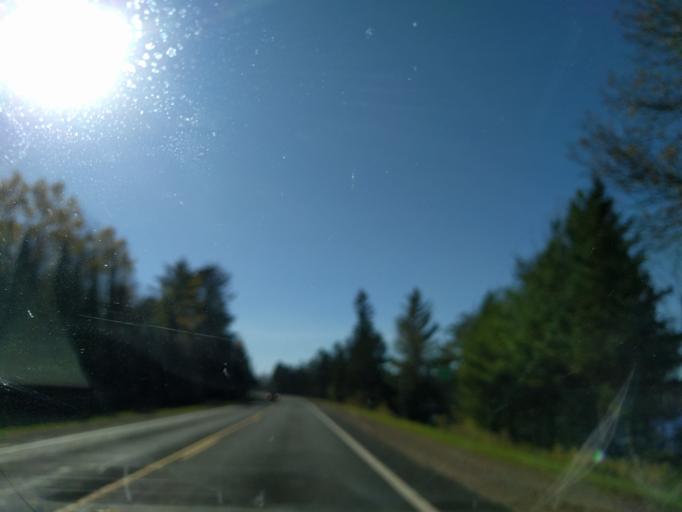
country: US
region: Michigan
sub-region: Iron County
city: Crystal Falls
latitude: 46.2013
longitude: -88.0164
